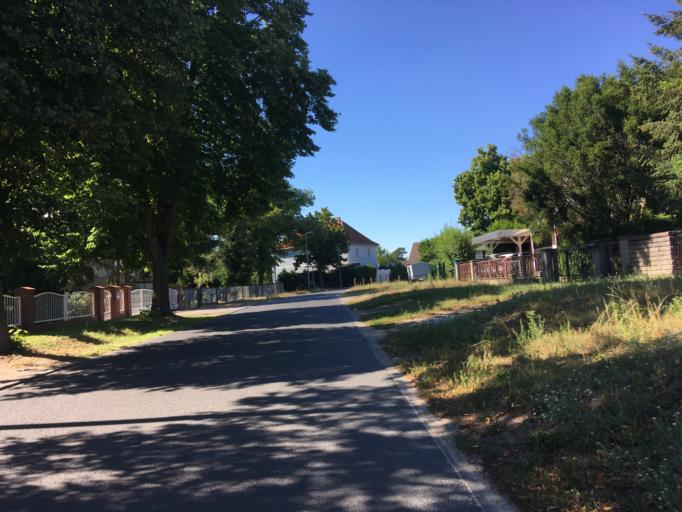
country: DE
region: Brandenburg
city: Schulzendorf
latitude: 52.3701
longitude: 13.5941
